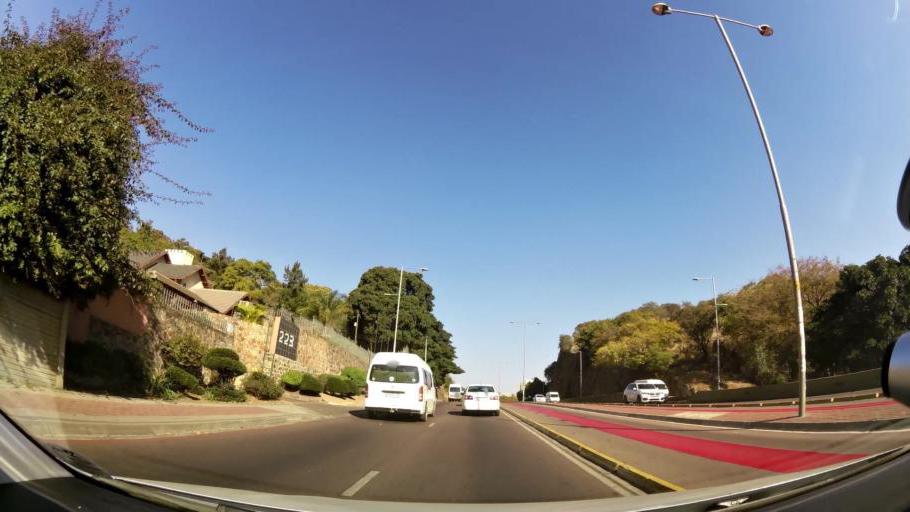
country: ZA
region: Gauteng
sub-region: City of Tshwane Metropolitan Municipality
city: Pretoria
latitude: -25.7303
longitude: 28.1892
